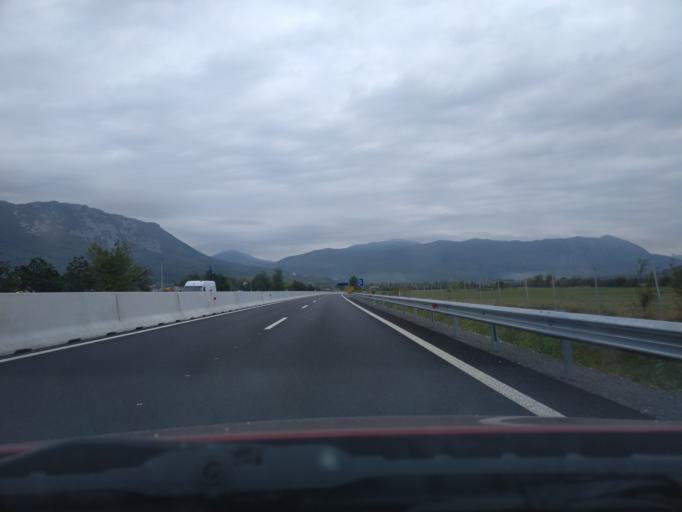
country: SI
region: Ajdovscina
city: Ajdovscina
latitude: 45.8829
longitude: 13.8898
